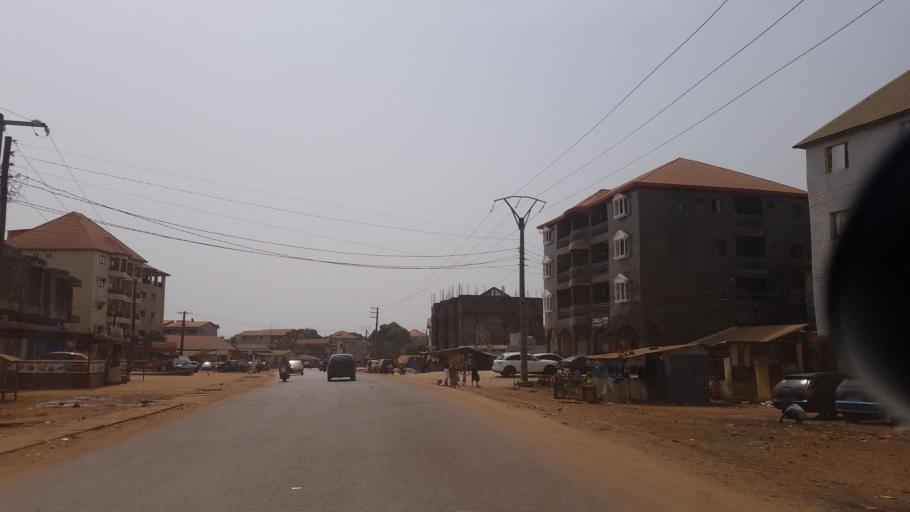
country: GN
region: Kindia
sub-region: Prefecture de Dubreka
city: Dubreka
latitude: 9.6814
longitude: -13.5724
